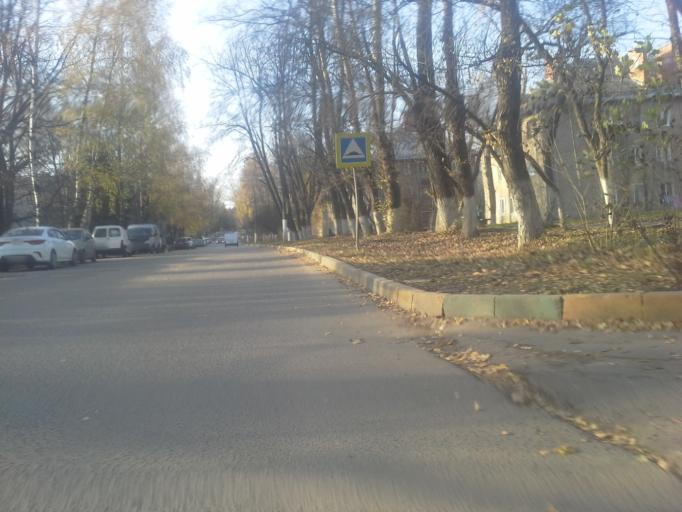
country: RU
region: Moskovskaya
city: Golitsyno
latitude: 55.5665
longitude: 36.9928
